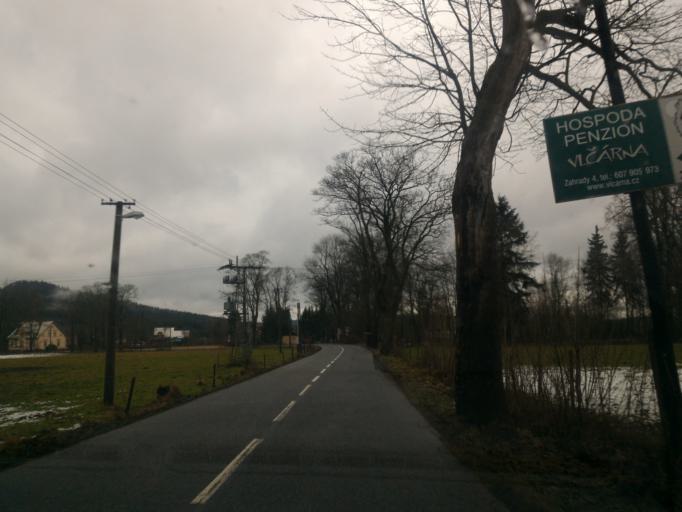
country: CZ
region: Ustecky
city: Stare Krecany
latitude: 50.9322
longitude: 14.4830
